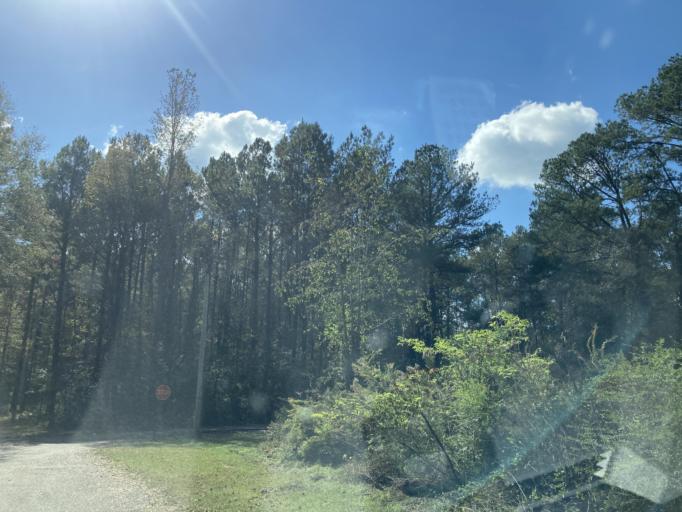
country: US
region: Mississippi
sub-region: Lamar County
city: West Hattiesburg
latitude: 31.2409
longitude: -89.4313
